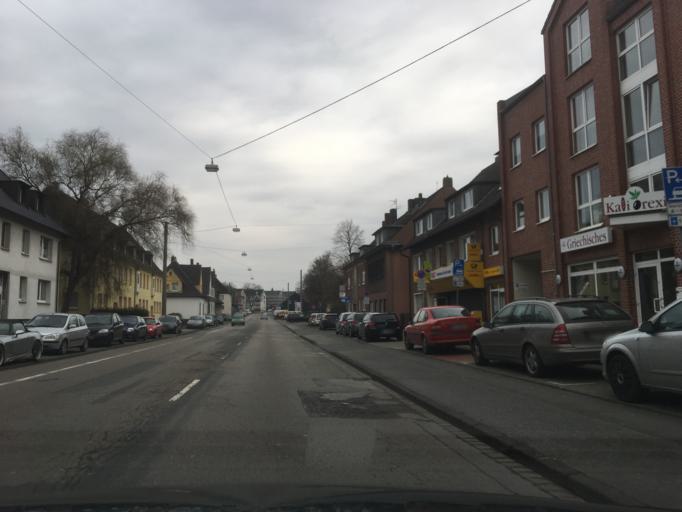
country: DE
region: North Rhine-Westphalia
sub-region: Regierungsbezirk Munster
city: Bottrop
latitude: 51.5304
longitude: 6.9439
